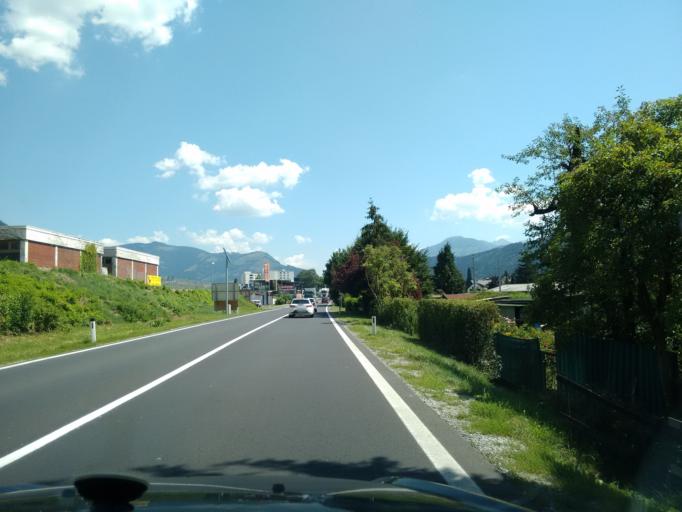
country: AT
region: Styria
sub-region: Politischer Bezirk Liezen
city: Liezen
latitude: 47.5667
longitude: 14.2339
